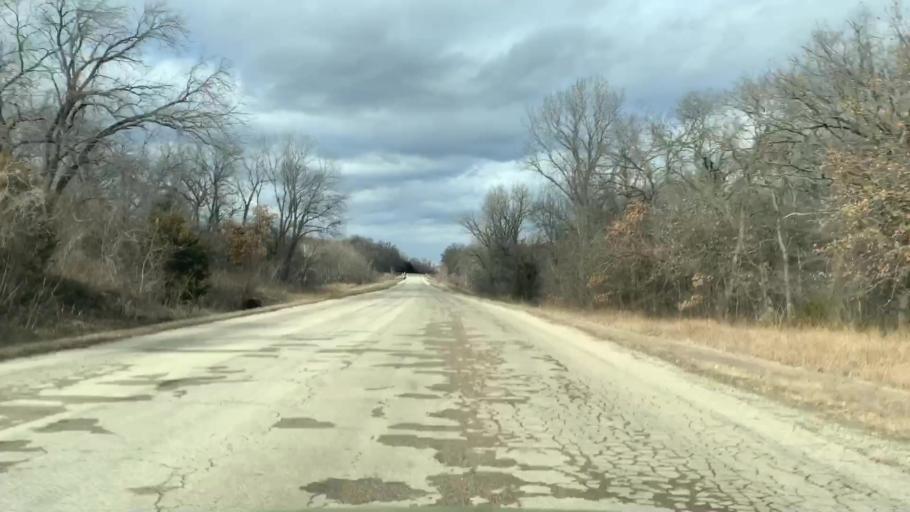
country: US
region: Kansas
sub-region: Allen County
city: Humboldt
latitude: 37.7505
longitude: -95.4704
